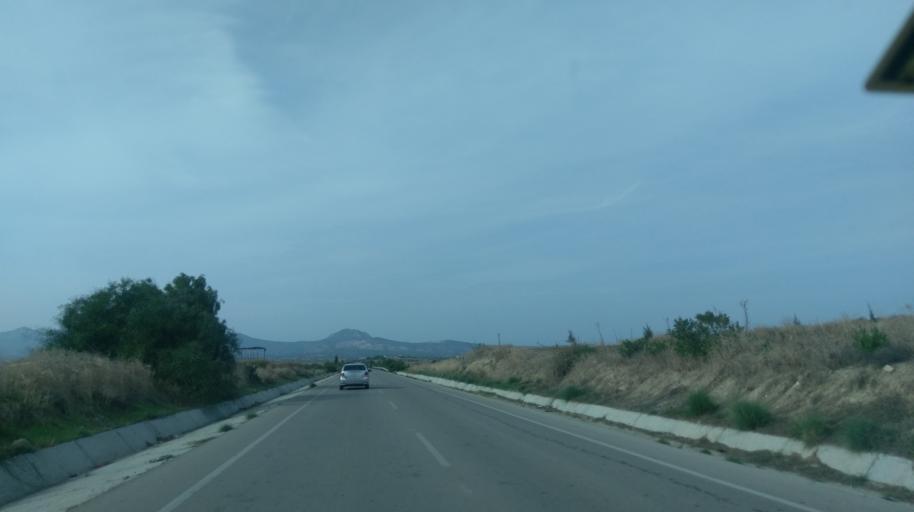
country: CY
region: Ammochostos
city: Leonarisso
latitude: 35.3771
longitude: 34.0264
